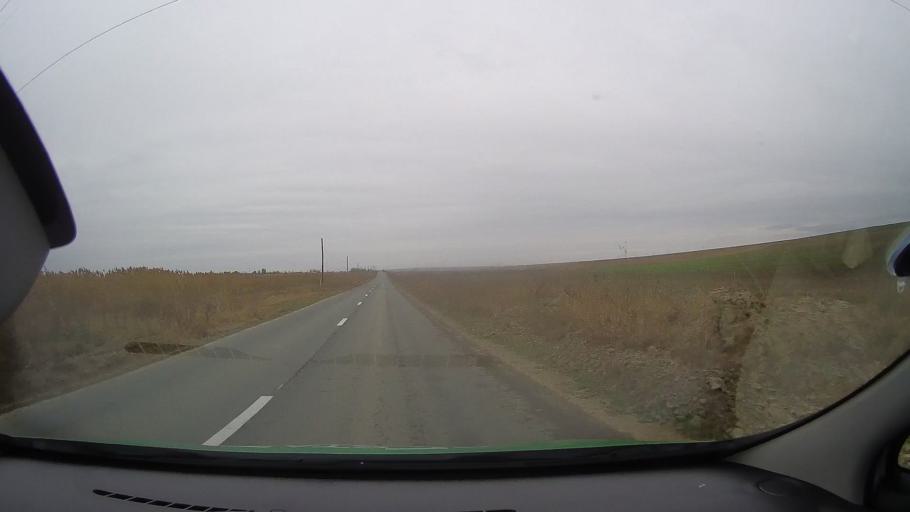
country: RO
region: Constanta
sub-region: Comuna Silistea
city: Silistea
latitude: 44.4357
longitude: 28.2225
